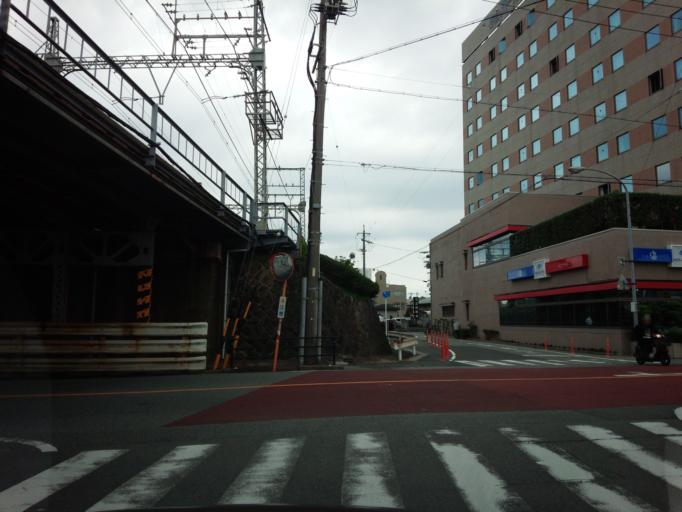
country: JP
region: Mie
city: Ise
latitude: 34.4913
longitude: 136.7127
